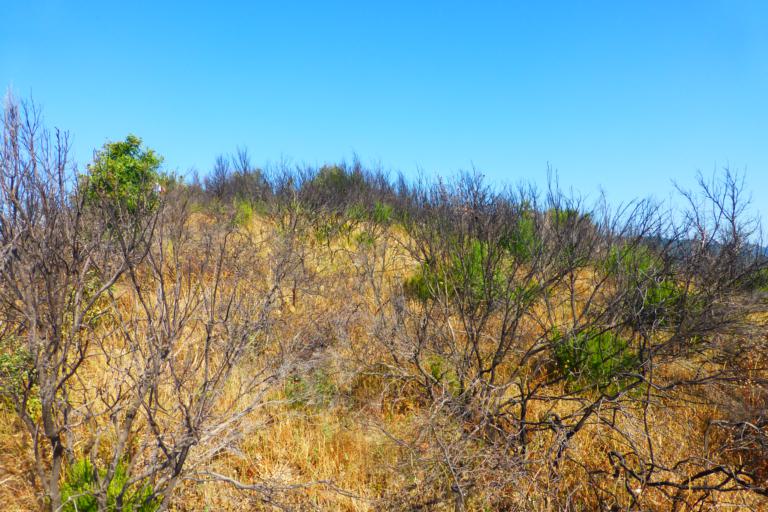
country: IT
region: Calabria
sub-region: Provincia di Reggio Calabria
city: Bivongi
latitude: 38.5021
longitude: 16.4437
